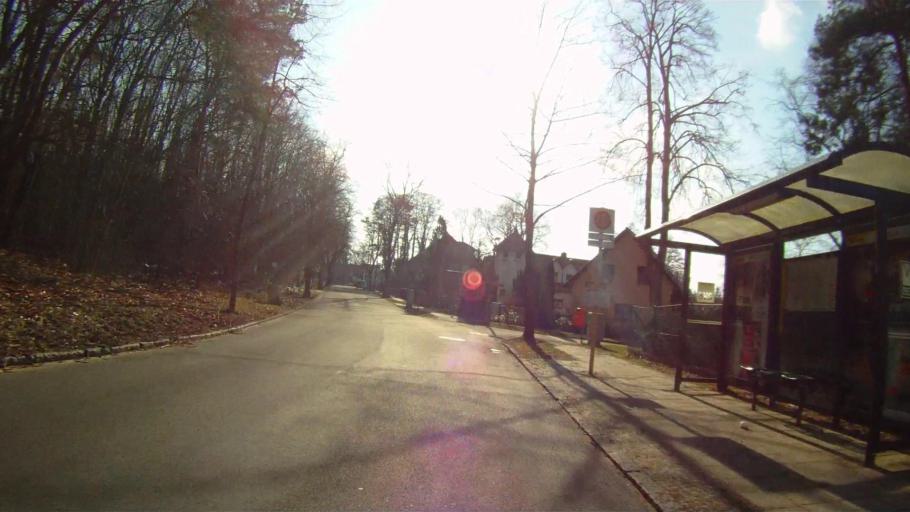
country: DE
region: Berlin
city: Rahnsdorf
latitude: 52.4271
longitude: 13.7192
